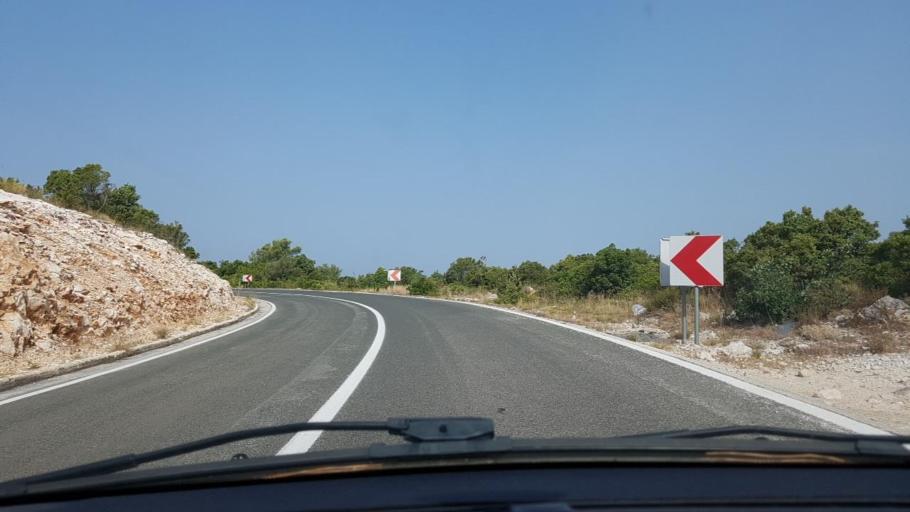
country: HR
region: Dubrovacko-Neretvanska
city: Podgora
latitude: 42.7707
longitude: 17.8776
